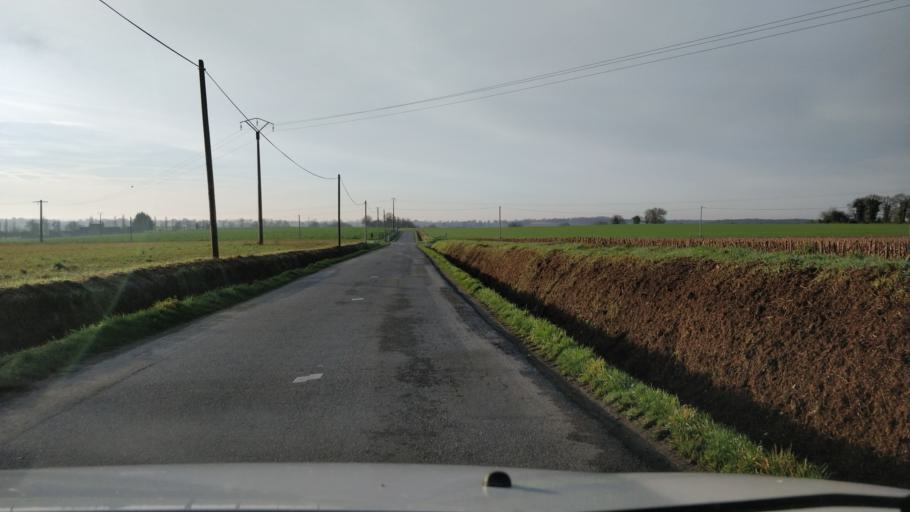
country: FR
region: Brittany
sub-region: Departement d'Ille-et-Vilaine
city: Louvigne-de-Bais
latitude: 48.0177
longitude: -1.3231
